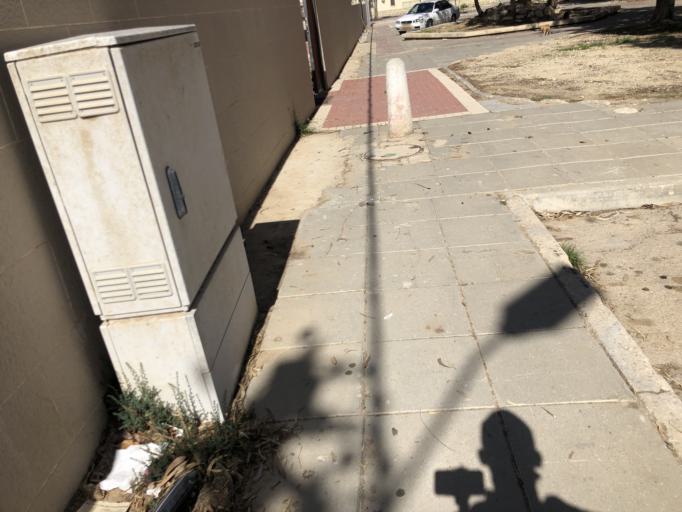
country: IL
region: Southern District
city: Dimona
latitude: 31.0663
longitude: 35.0367
